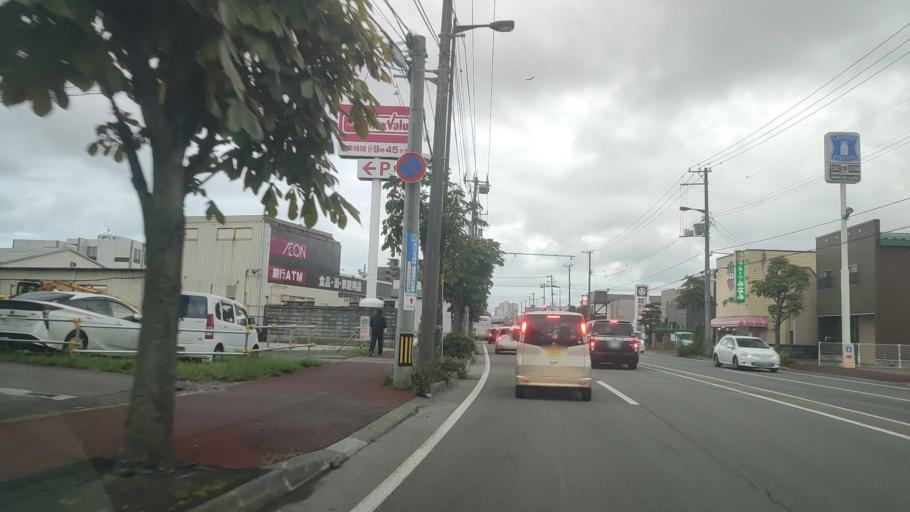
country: JP
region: Hokkaido
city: Hakodate
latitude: 41.7863
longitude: 140.7306
